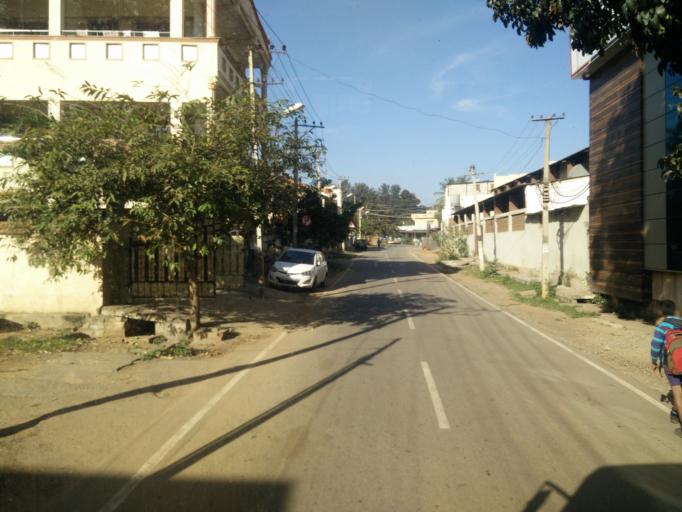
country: IN
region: Karnataka
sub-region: Bangalore Urban
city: Yelahanka
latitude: 13.0967
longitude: 77.5969
